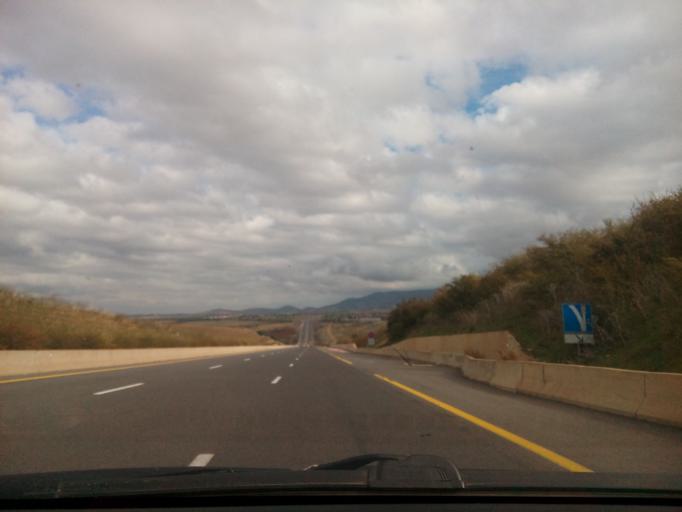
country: DZ
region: Tlemcen
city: Chetouane
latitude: 34.9790
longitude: -1.2501
